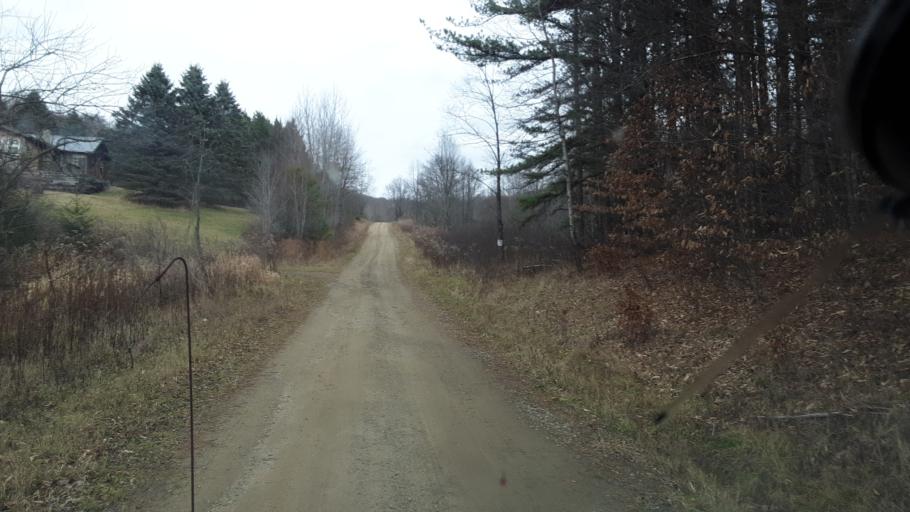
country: US
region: Pennsylvania
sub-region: Tioga County
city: Westfield
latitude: 41.9121
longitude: -77.7072
